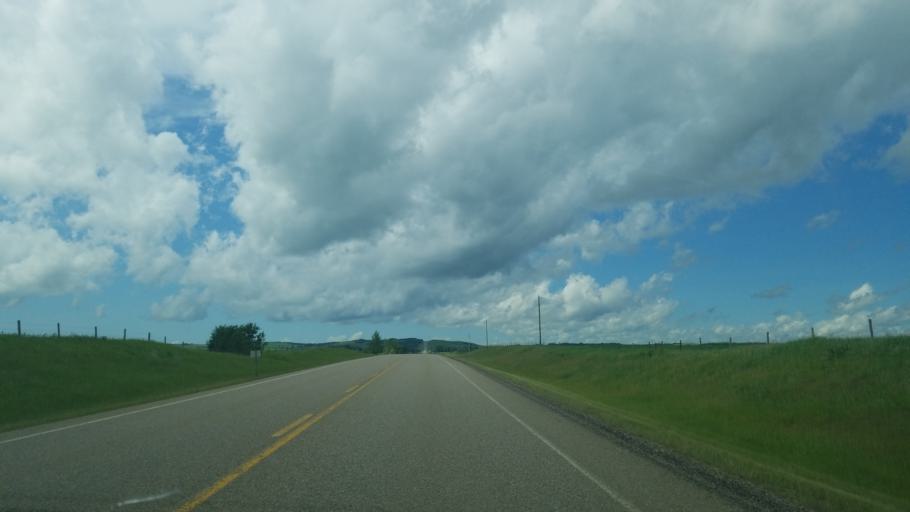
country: CA
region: Saskatchewan
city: Lloydminster
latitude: 53.1617
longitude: -110.1772
